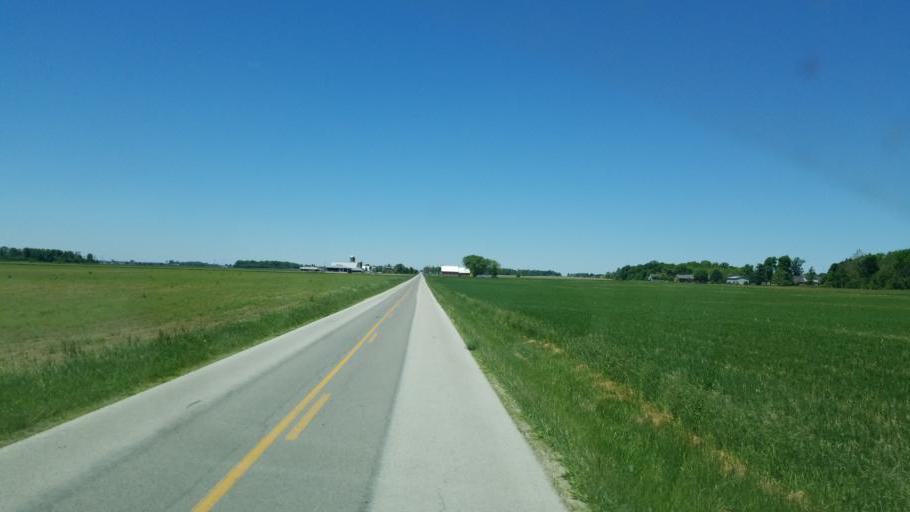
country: US
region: Ohio
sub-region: Auglaize County
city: Minster
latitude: 40.3786
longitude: -84.4686
